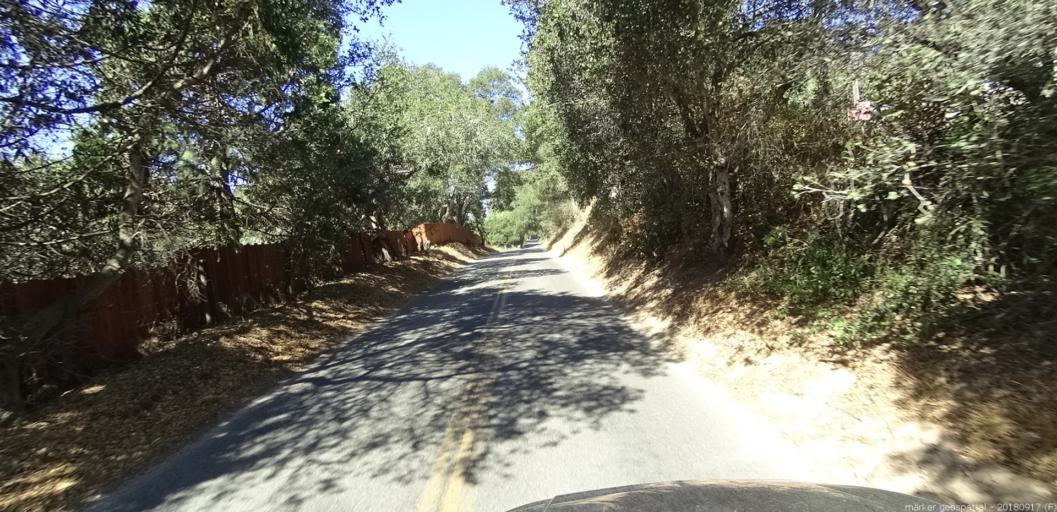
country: US
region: California
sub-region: Monterey County
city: Elkhorn
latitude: 36.8255
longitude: -121.7243
